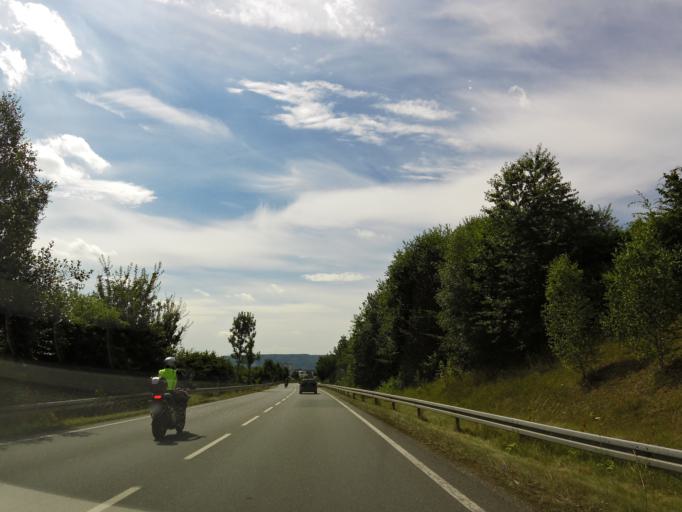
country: DE
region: North Rhine-Westphalia
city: Beverungen
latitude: 51.6898
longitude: 9.3786
